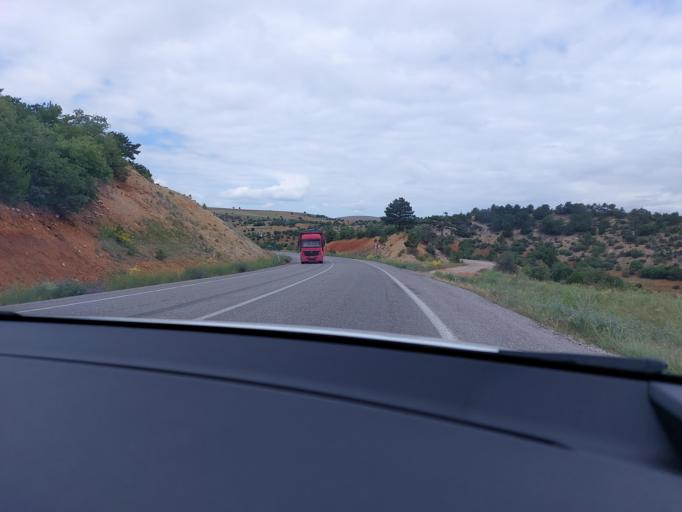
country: TR
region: Konya
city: Doganbey
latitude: 37.8978
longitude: 31.8064
